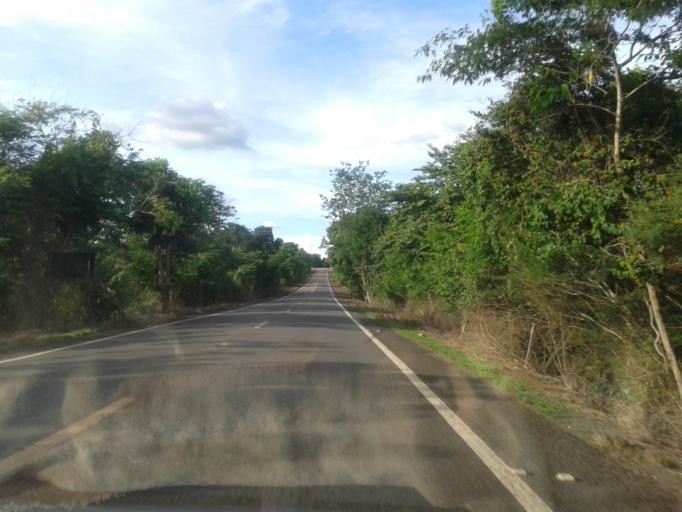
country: BR
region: Goias
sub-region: Crixas
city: Crixas
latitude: -13.9828
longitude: -50.3227
